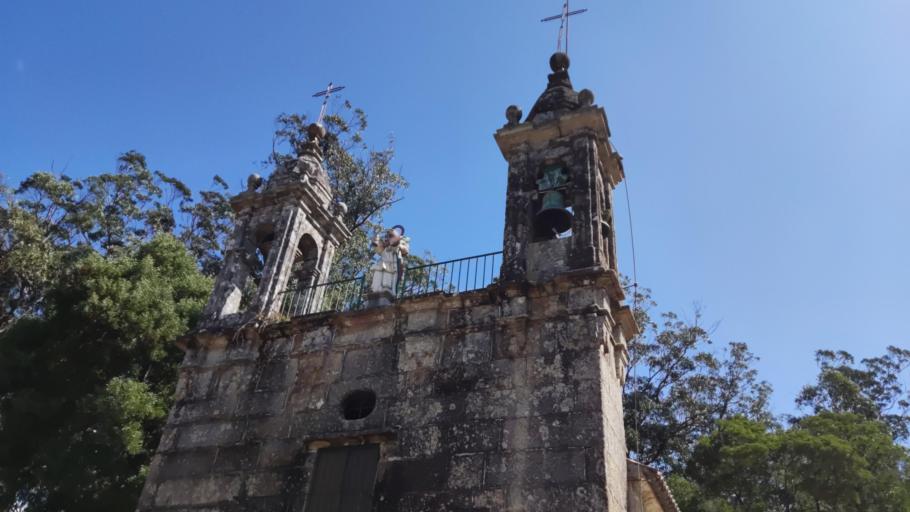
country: ES
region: Galicia
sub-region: Provincia da Coruna
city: Rianxo
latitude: 42.7007
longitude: -8.8452
